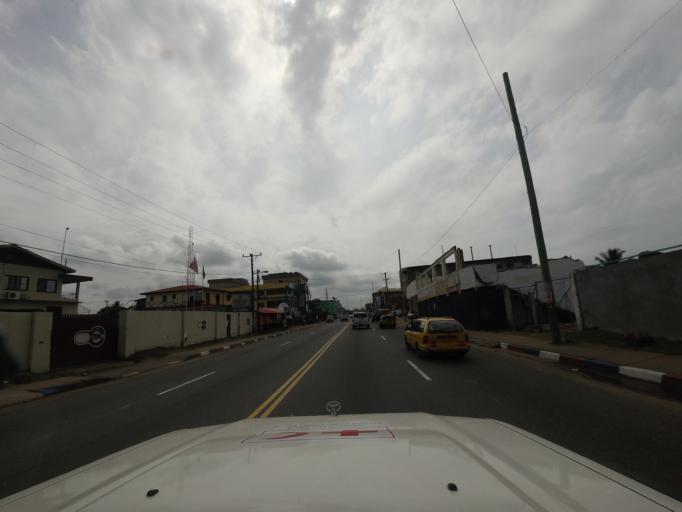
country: LR
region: Montserrado
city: Monrovia
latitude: 6.2946
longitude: -10.7920
